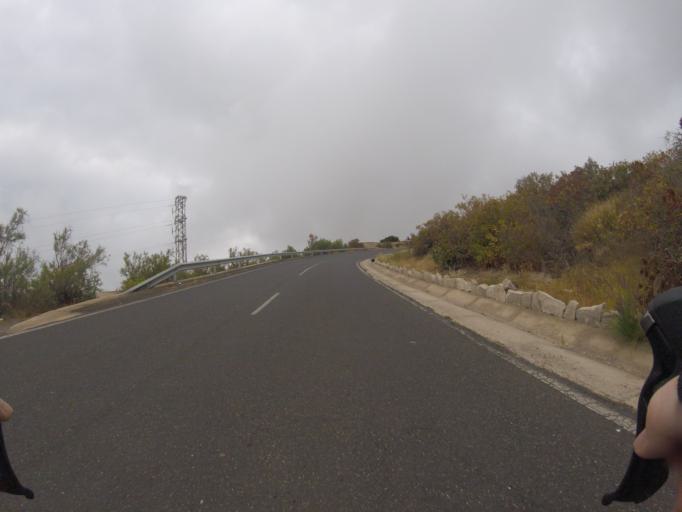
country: ES
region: Canary Islands
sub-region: Provincia de Santa Cruz de Tenerife
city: Guimar
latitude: 28.2901
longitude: -16.4020
